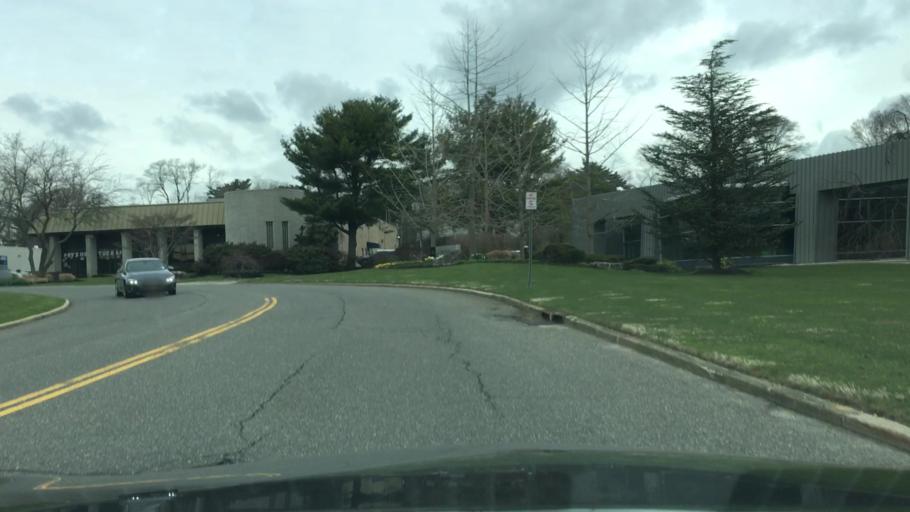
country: US
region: New York
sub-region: Nassau County
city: Woodbury
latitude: 40.8079
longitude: -73.4823
